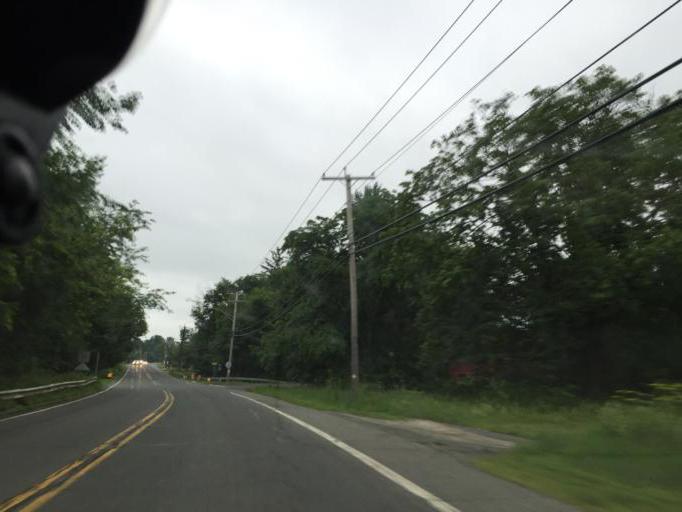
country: US
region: Massachusetts
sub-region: Berkshire County
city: Sheffield
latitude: 42.0960
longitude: -73.3515
